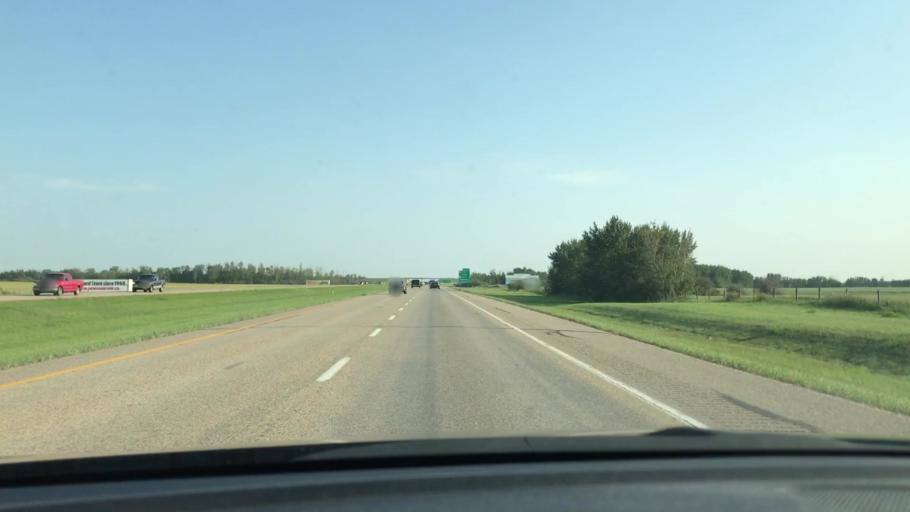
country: CA
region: Alberta
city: Millet
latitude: 53.1046
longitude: -113.5984
